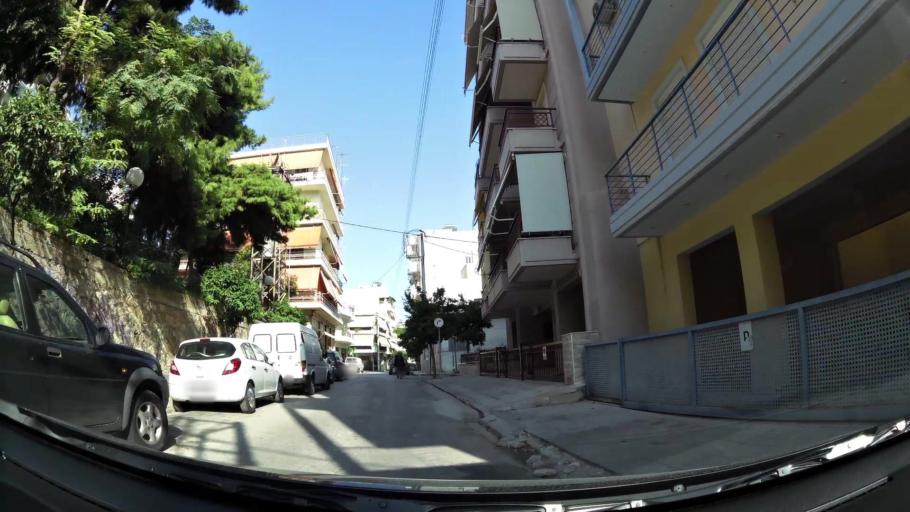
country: GR
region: Attica
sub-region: Nomos Piraios
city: Drapetsona
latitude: 37.9545
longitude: 23.6202
